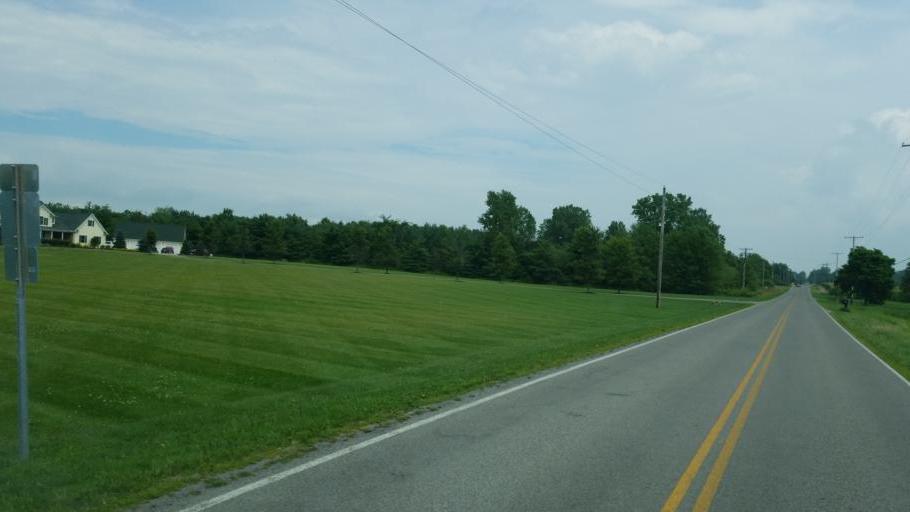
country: US
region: Ohio
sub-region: Logan County
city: Northwood
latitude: 40.4185
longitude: -83.7508
